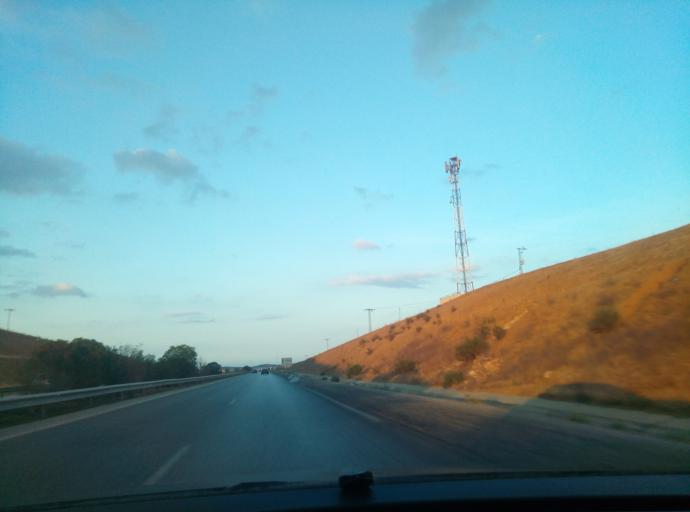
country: TN
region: Tunis
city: Oued Lill
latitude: 36.7291
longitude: 10.0049
